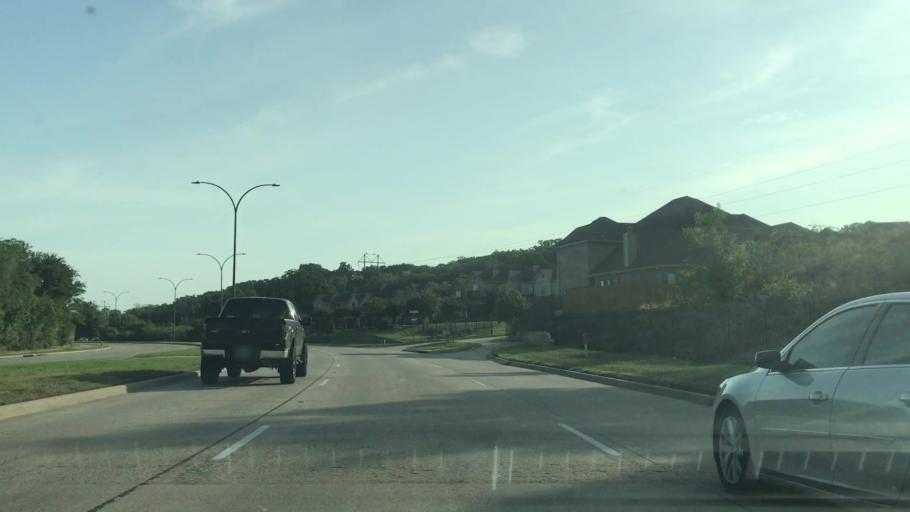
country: US
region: Texas
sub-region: Tarrant County
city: Arlington
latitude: 32.7724
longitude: -97.1375
